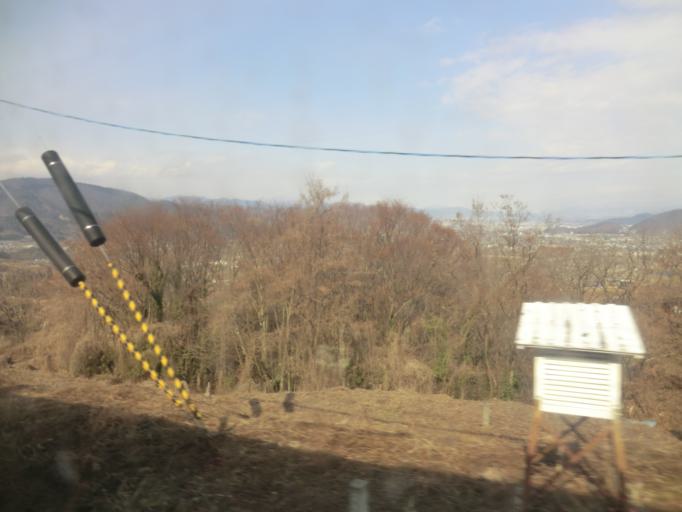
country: JP
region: Nagano
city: Nagano-shi
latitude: 36.5006
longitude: 138.0963
